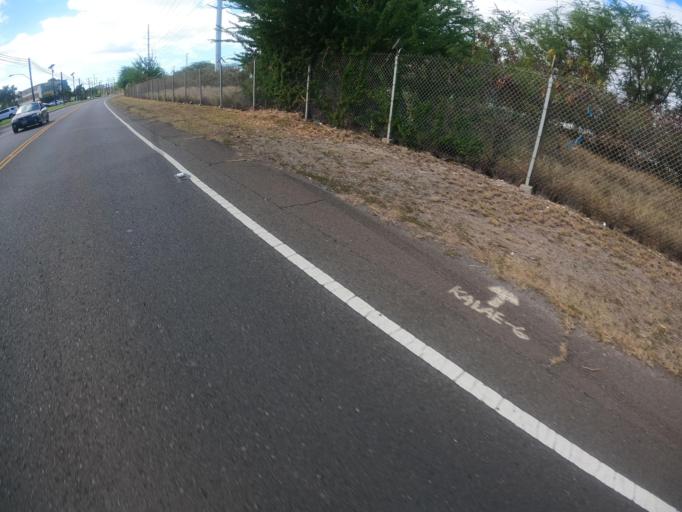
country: US
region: Hawaii
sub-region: Honolulu County
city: Makakilo City
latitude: 21.3228
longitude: -158.0761
